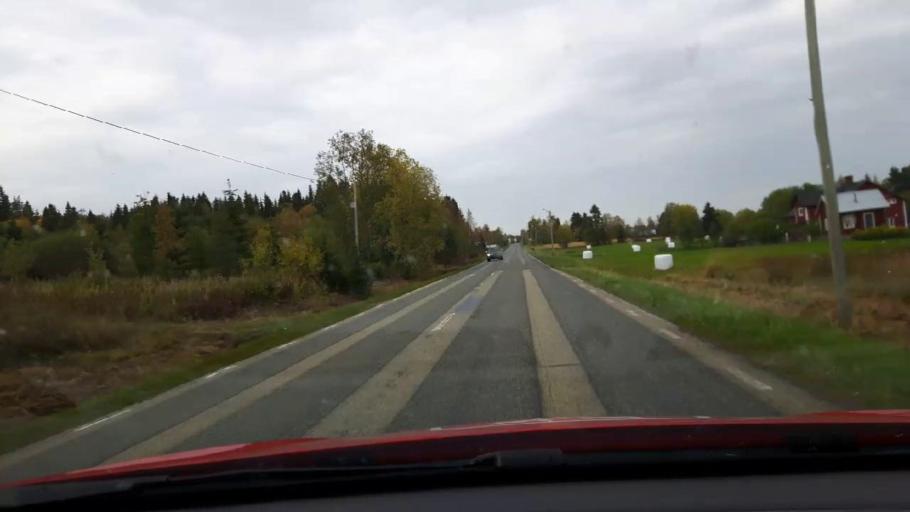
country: SE
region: Jaemtland
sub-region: Bergs Kommun
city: Hoverberg
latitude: 62.8268
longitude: 14.3904
